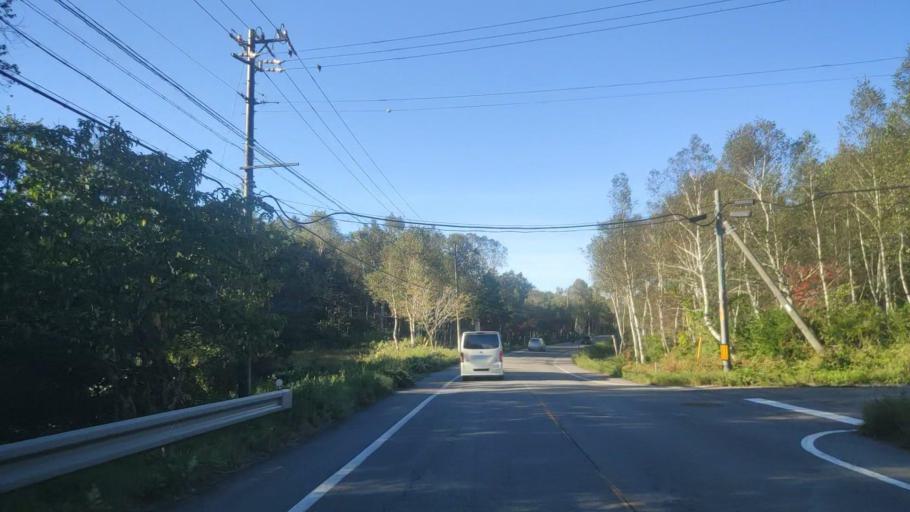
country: JP
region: Nagano
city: Kamimaruko
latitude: 36.1650
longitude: 138.2800
